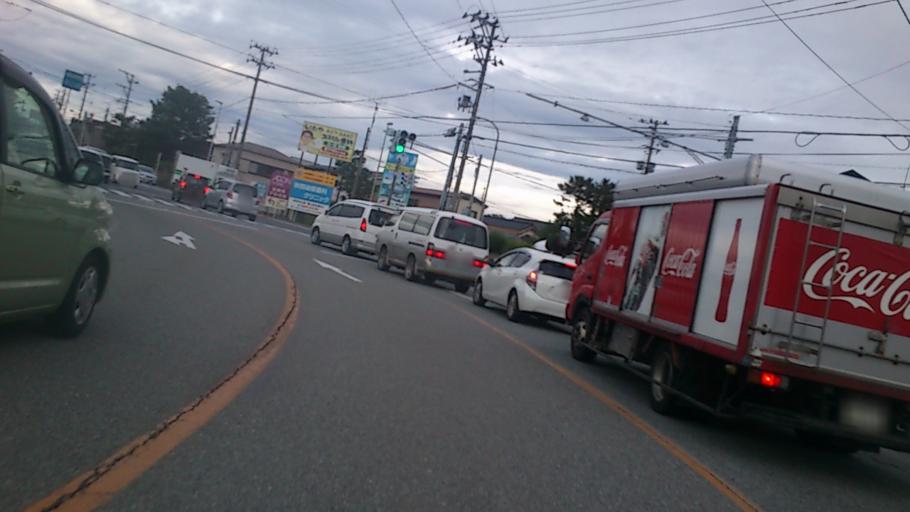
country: JP
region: Akita
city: Akita Shi
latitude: 39.7501
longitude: 140.0664
